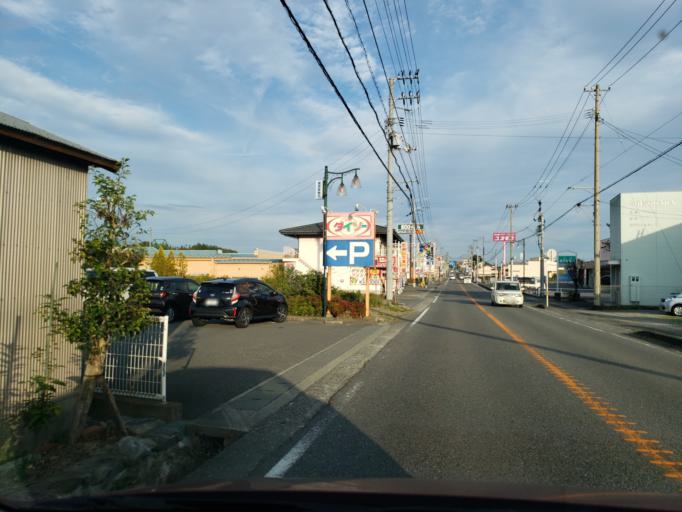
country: JP
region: Tokushima
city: Wakimachi
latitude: 34.0747
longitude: 134.2301
